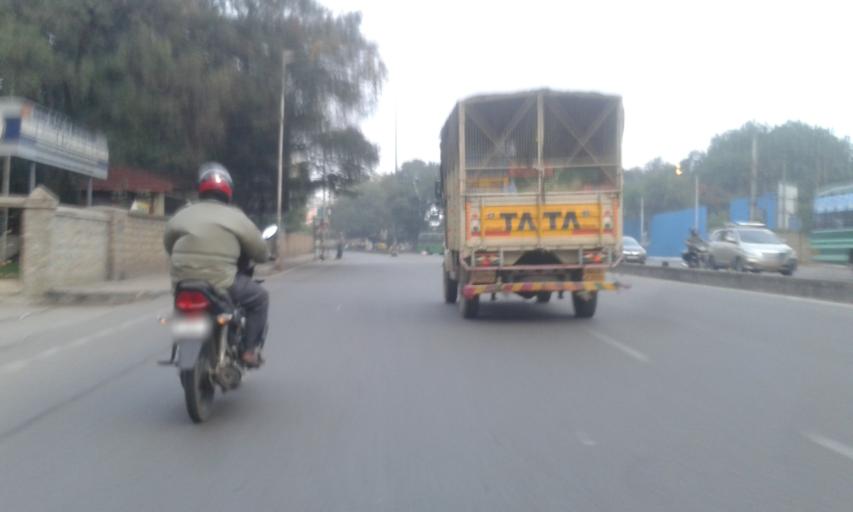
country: IN
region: Karnataka
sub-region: Bangalore Urban
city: Bangalore
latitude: 12.9308
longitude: 77.6142
